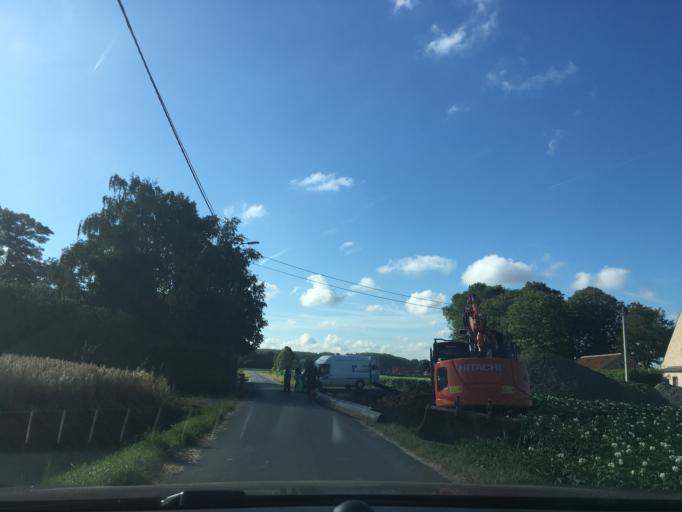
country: BE
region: Flanders
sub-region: Provincie West-Vlaanderen
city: Ardooie
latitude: 50.9675
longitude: 3.2206
